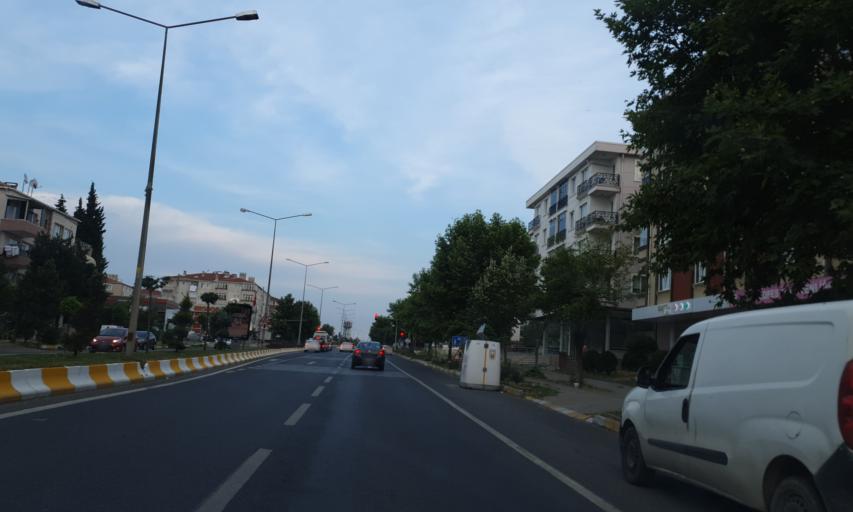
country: TR
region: Kirklareli
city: Luleburgaz
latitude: 41.4016
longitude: 27.3695
